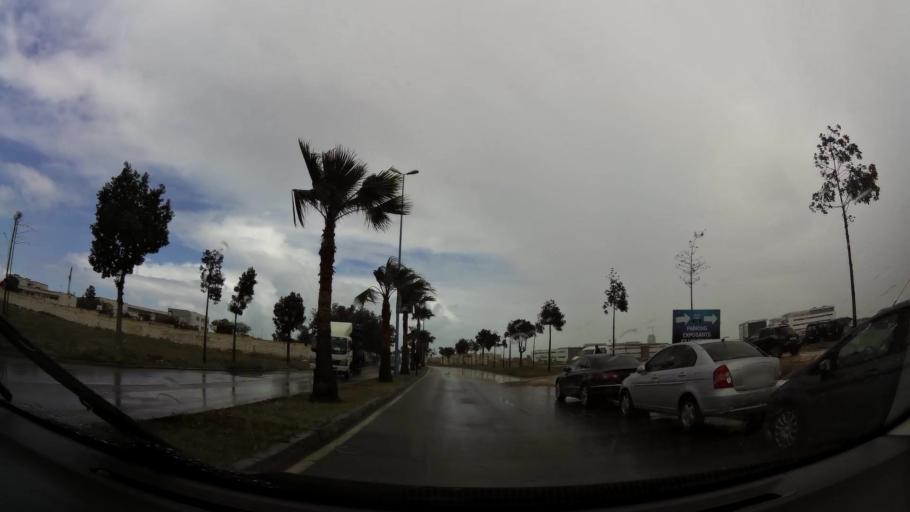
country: MA
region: Grand Casablanca
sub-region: Casablanca
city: Casablanca
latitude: 33.5485
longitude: -7.6700
